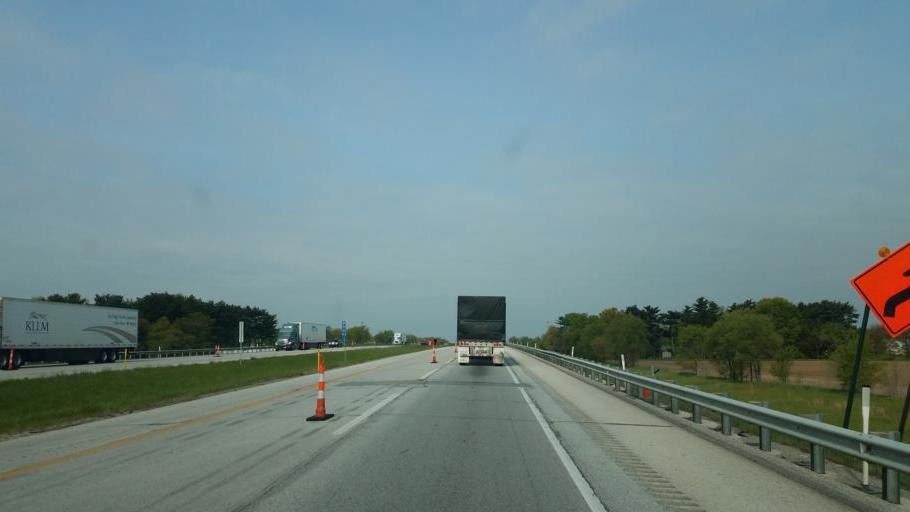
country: US
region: Indiana
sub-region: Elkhart County
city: Simonton Lake
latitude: 41.7305
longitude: -85.9426
